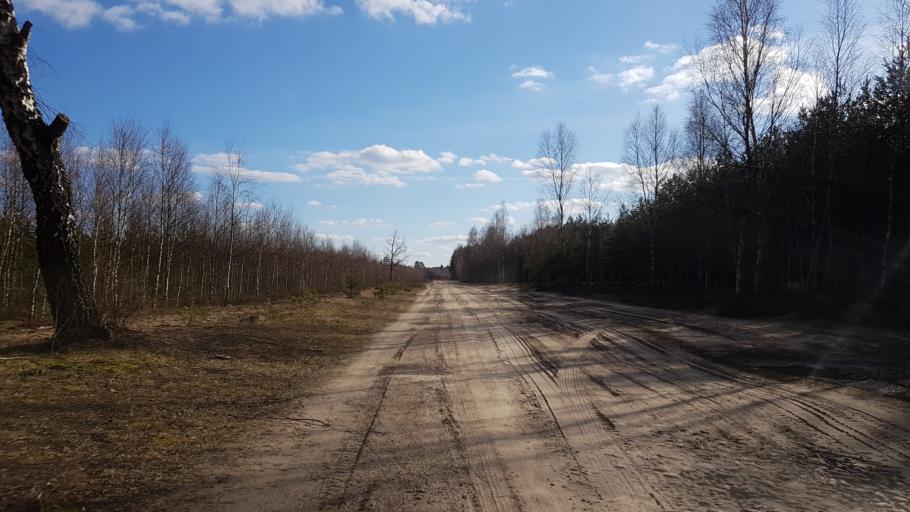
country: PL
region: Greater Poland Voivodeship
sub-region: Powiat zlotowski
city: Sypniewo
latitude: 53.5330
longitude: 16.6463
